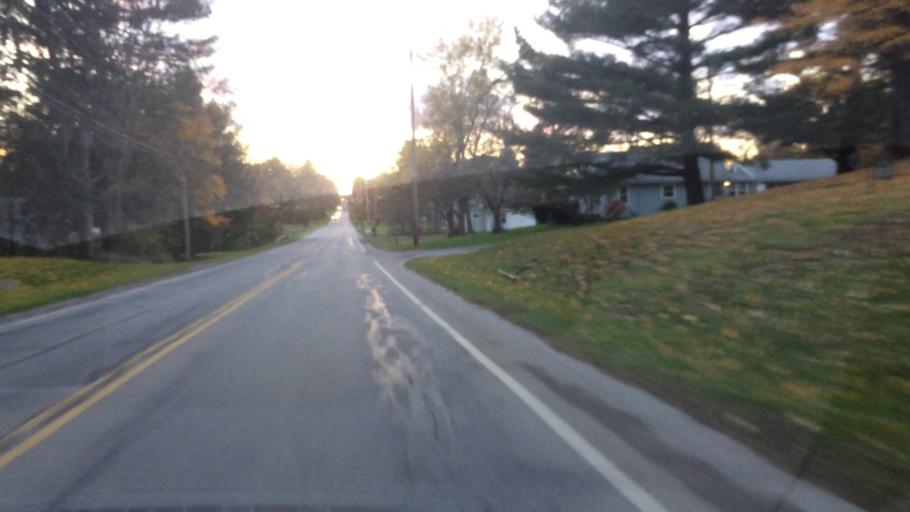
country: US
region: Ohio
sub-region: Summit County
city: Norton
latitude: 41.0502
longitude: -81.6445
